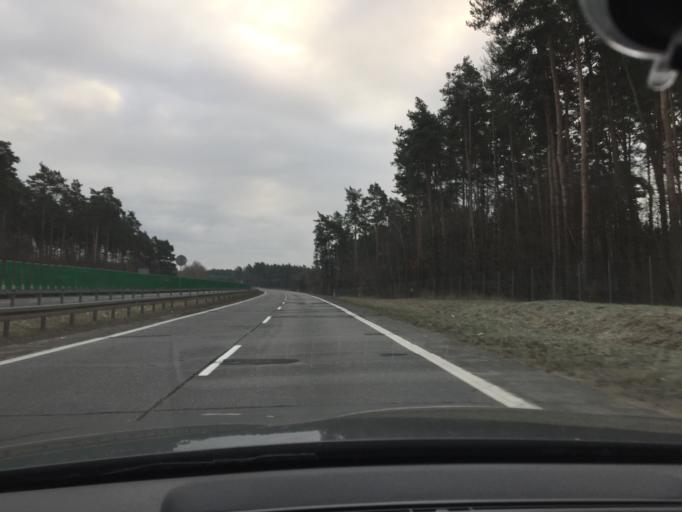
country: PL
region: Lubusz
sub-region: Powiat zarski
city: Trzebiel
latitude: 51.6476
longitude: 14.8299
